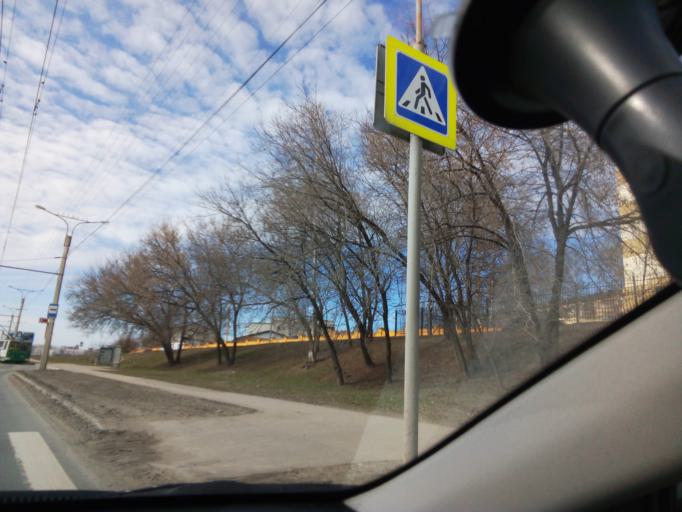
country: RU
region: Chuvashia
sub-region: Cheboksarskiy Rayon
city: Cheboksary
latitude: 56.1195
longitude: 47.2514
